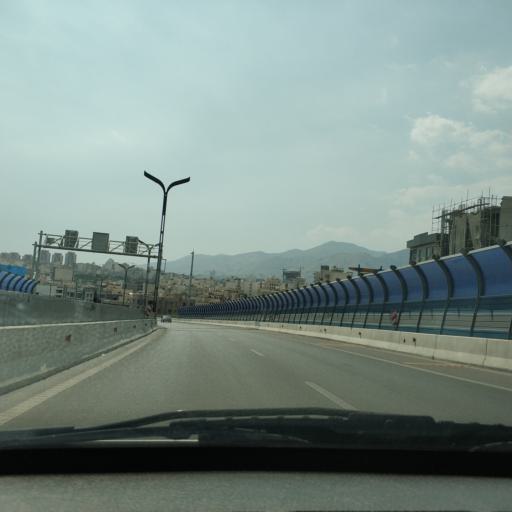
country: IR
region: Tehran
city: Tajrish
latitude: 35.7932
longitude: 51.4623
